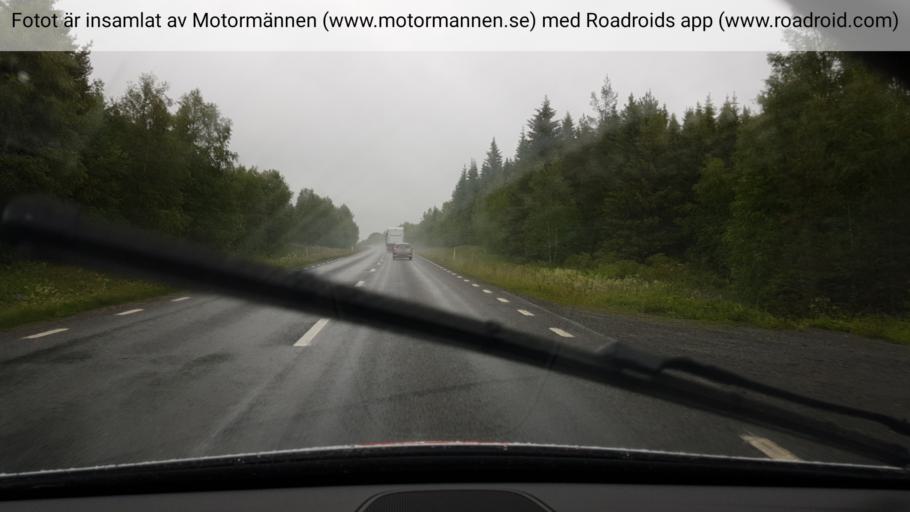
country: SE
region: Jaemtland
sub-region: OEstersunds Kommun
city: Lit
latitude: 63.4518
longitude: 15.1626
